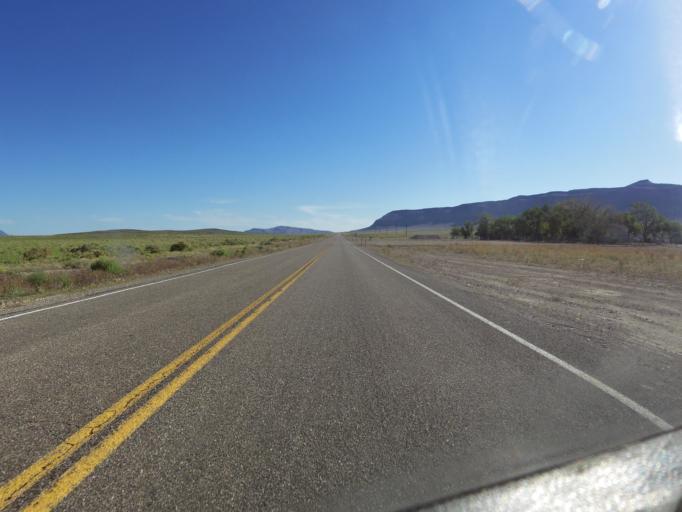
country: US
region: Nevada
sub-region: Nye County
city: Tonopah
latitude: 38.3711
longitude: -116.2274
